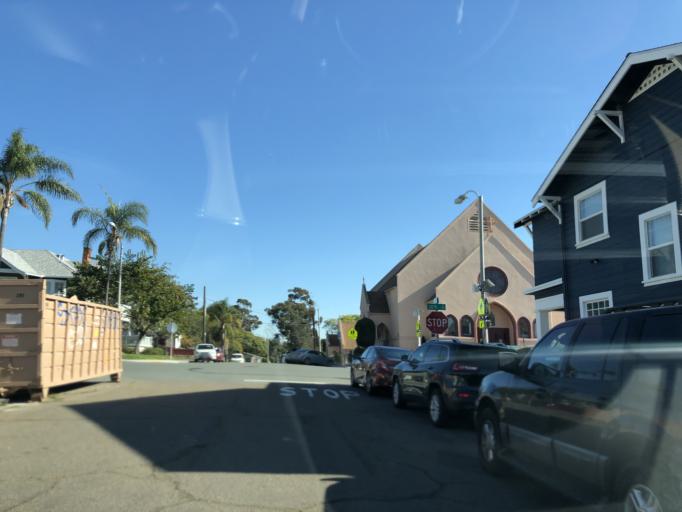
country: US
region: California
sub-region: San Diego County
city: San Diego
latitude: 32.7255
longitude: -117.1306
